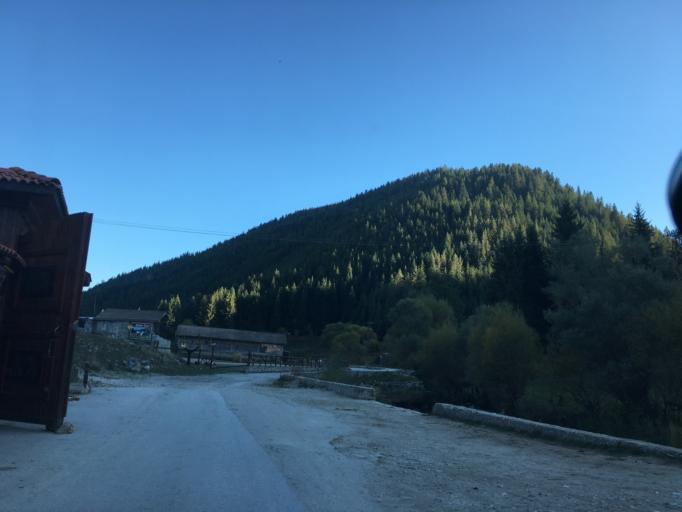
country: BG
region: Smolyan
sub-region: Obshtina Borino
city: Borino
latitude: 41.5841
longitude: 24.3927
